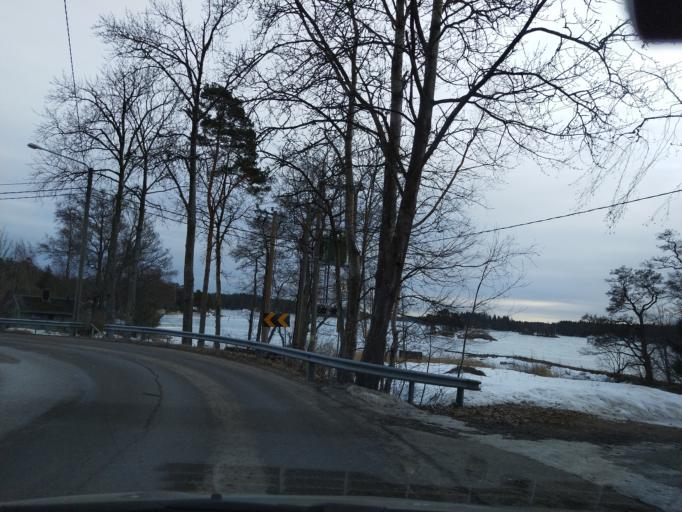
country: FI
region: Uusimaa
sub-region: Helsinki
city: Sibbo
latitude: 60.2563
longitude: 25.2917
